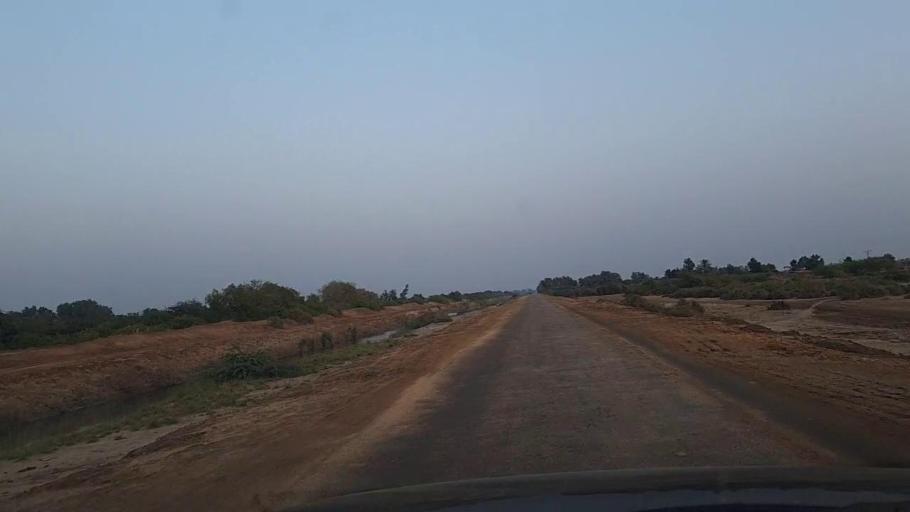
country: PK
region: Sindh
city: Mirpur Sakro
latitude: 24.6325
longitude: 67.6241
